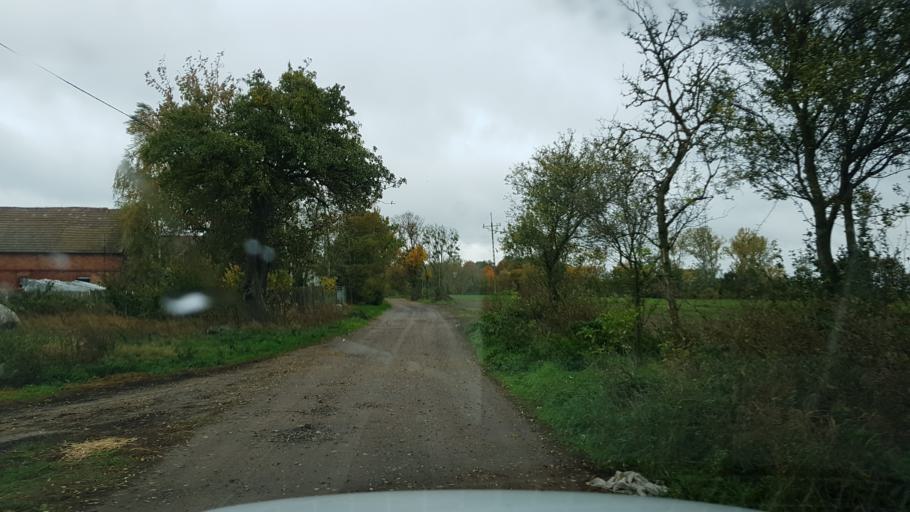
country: PL
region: West Pomeranian Voivodeship
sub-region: Powiat pyrzycki
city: Lipiany
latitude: 52.9734
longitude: 15.0106
